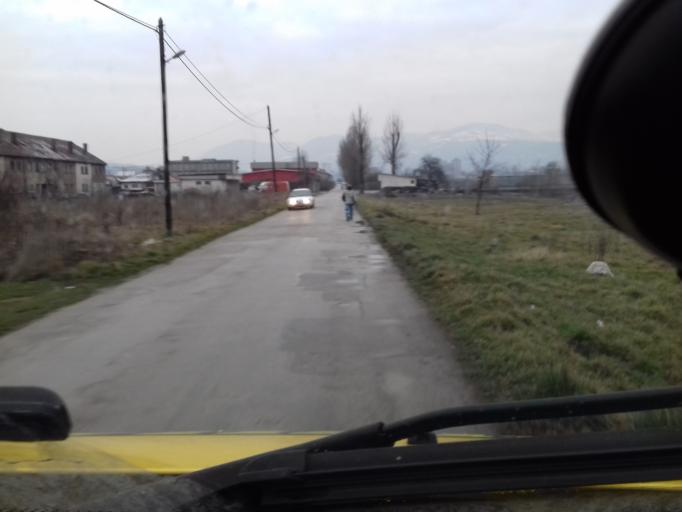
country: BA
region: Federation of Bosnia and Herzegovina
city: Zenica
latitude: 44.2232
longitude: 17.9080
